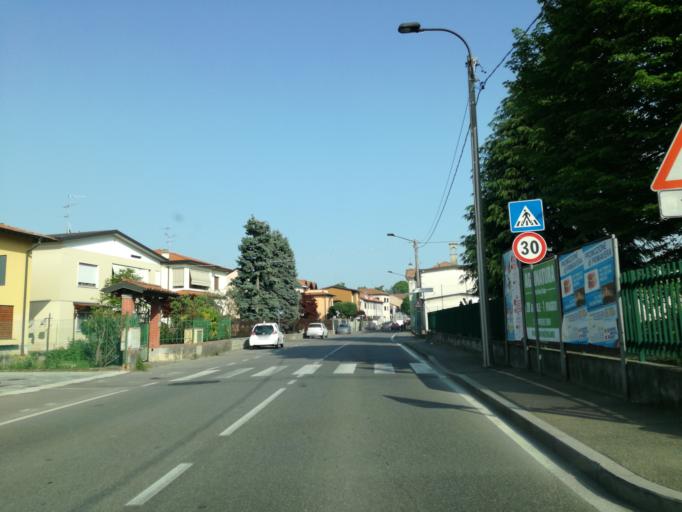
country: IT
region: Lombardy
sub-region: Provincia di Lecco
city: Verderio Inferiore
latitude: 45.6624
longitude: 9.4319
